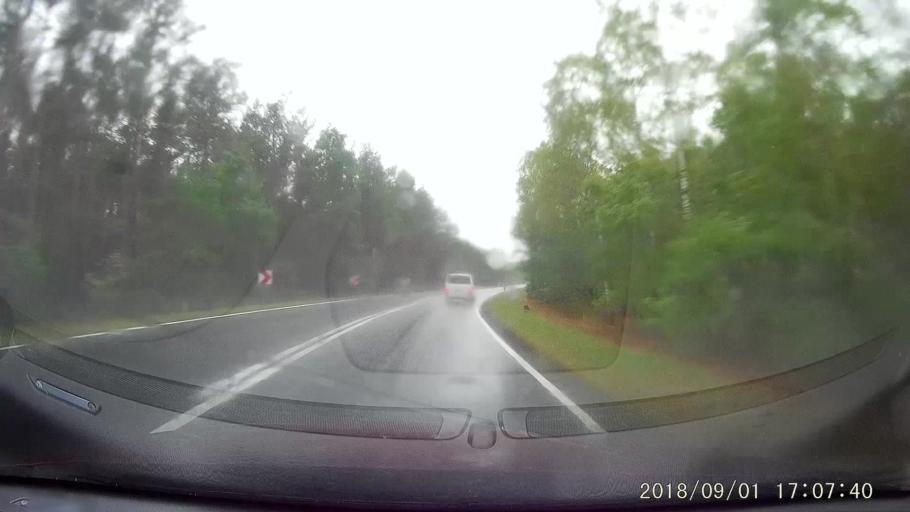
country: PL
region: Lubusz
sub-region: Powiat zielonogorski
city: Swidnica
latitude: 51.8348
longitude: 15.3191
